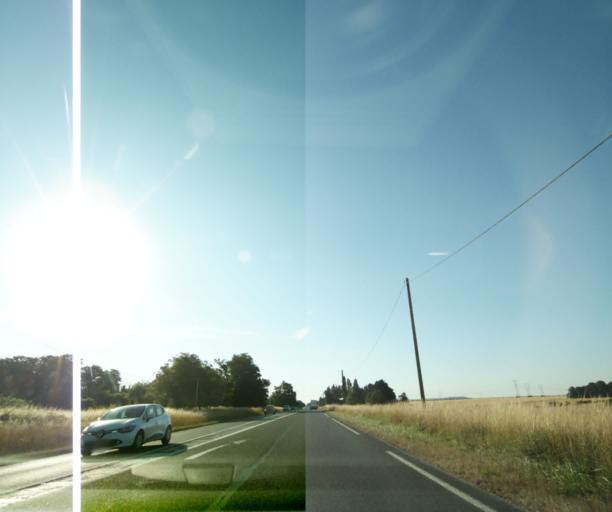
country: FR
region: Ile-de-France
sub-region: Departement de Seine-et-Marne
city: Vernou-la-Celle-sur-Seine
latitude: 48.3654
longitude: 2.8489
